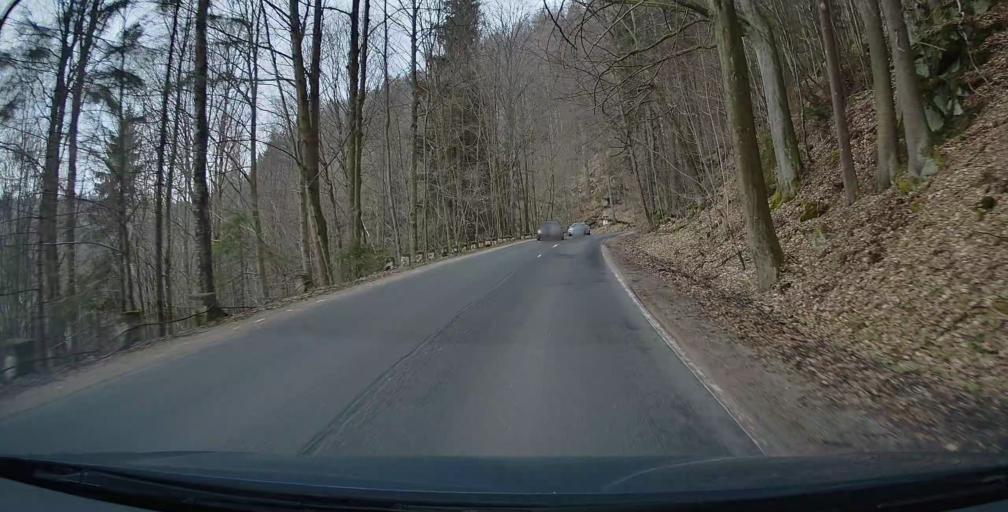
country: PL
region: Lower Silesian Voivodeship
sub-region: Powiat klodzki
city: Radkow
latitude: 50.4815
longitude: 16.3851
